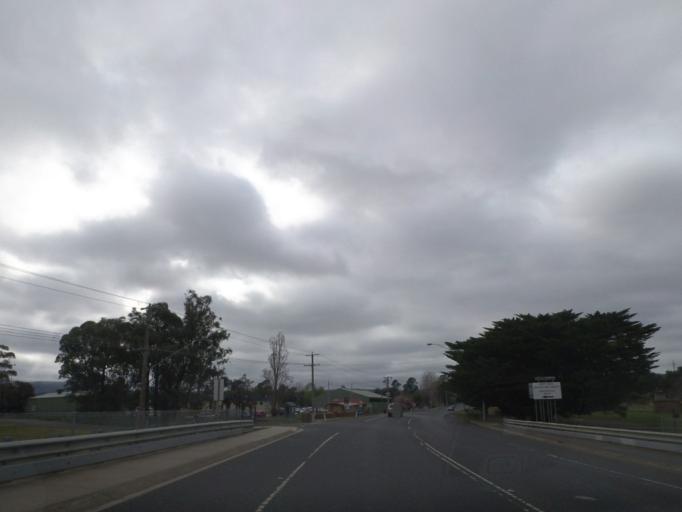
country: AU
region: Victoria
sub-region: Whittlesea
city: Whittlesea
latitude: -37.5107
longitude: 145.1246
